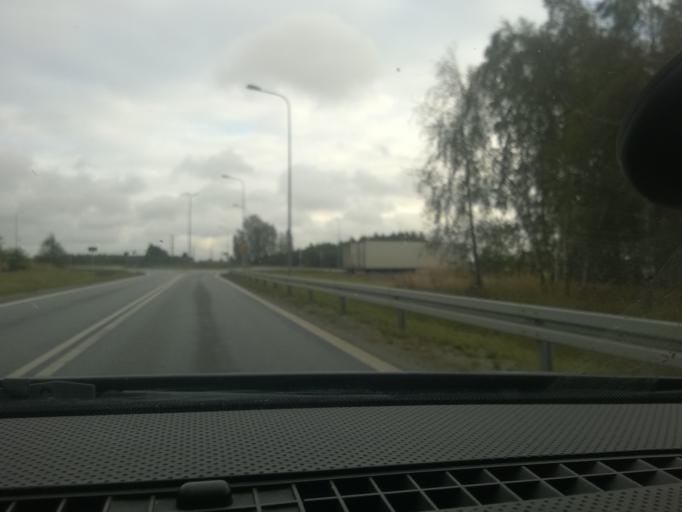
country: PL
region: Lodz Voivodeship
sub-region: Powiat sieradzki
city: Sieradz
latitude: 51.5815
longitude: 18.6713
